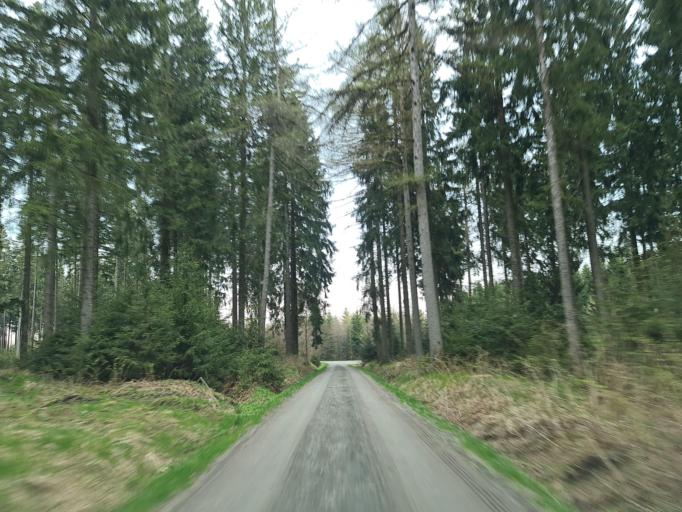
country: DE
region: Saxony
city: Ellefeld
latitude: 50.4603
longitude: 12.3992
